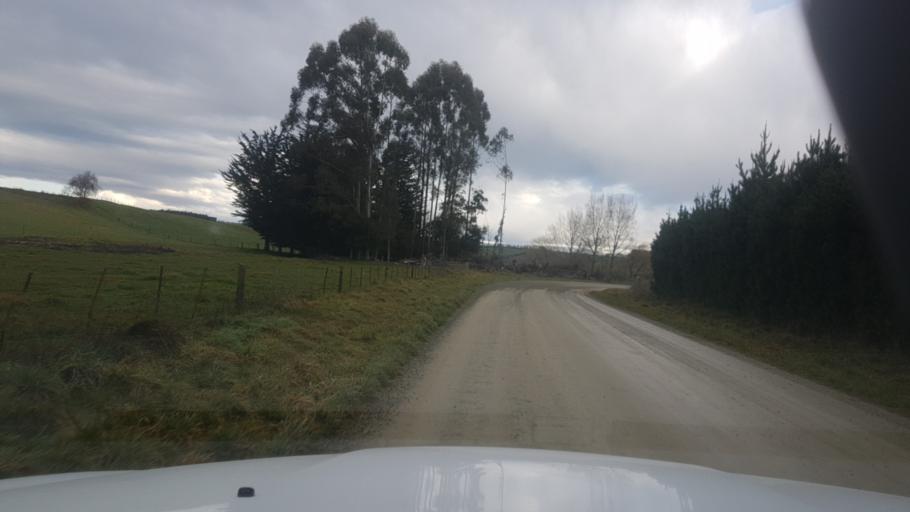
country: NZ
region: Canterbury
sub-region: Timaru District
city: Pleasant Point
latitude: -44.3380
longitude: 171.1813
